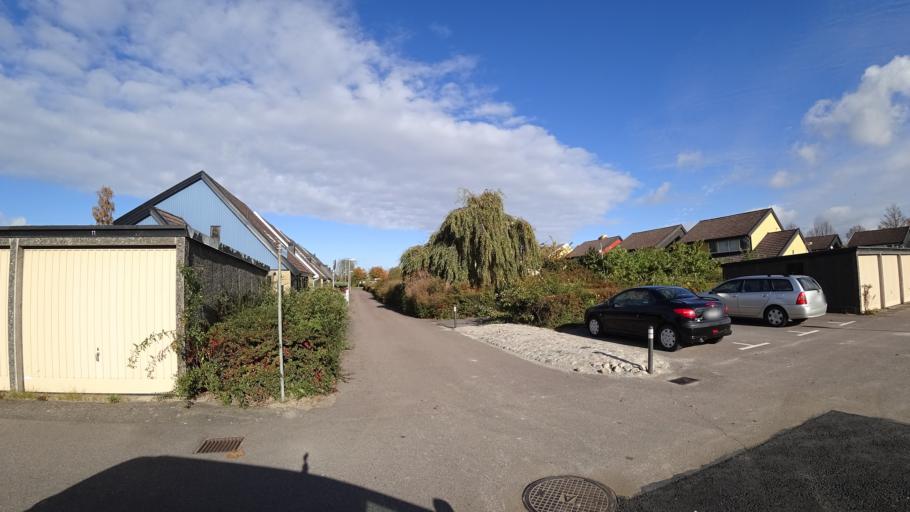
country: SE
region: Skane
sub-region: Staffanstorps Kommun
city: Staffanstorp
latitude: 55.6332
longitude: 13.1973
